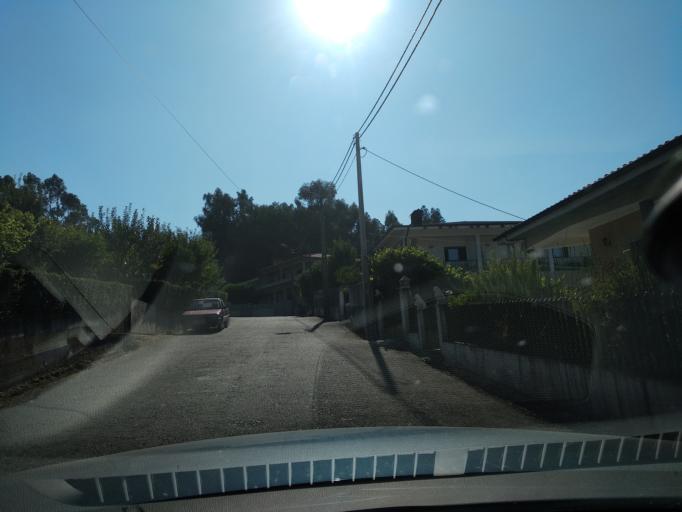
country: PT
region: Porto
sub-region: Paredes
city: Baltar
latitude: 41.2089
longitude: -8.3683
